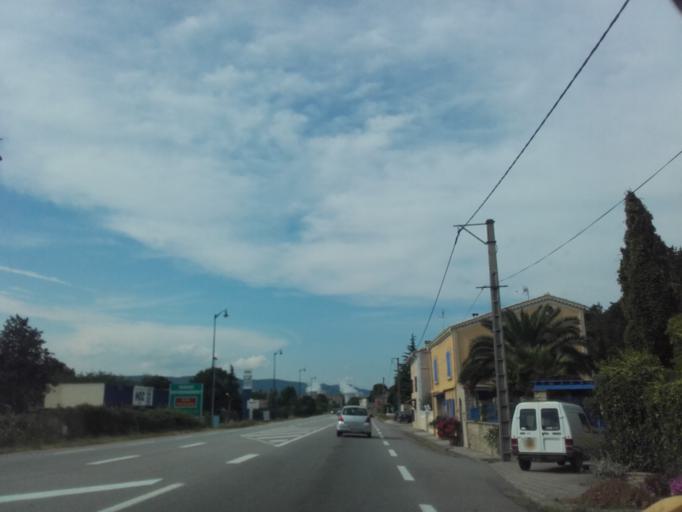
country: FR
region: Rhone-Alpes
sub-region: Departement de la Drome
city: Ancone
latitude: 44.5896
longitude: 4.7518
